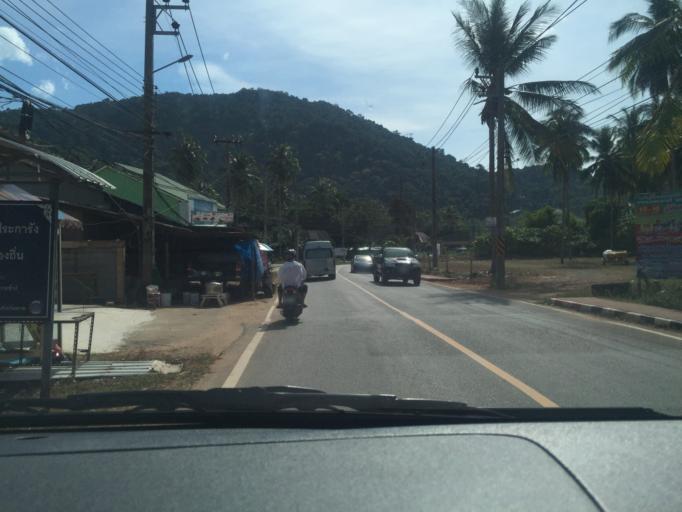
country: TH
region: Trat
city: Laem Ngop
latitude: 12.1312
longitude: 102.2751
